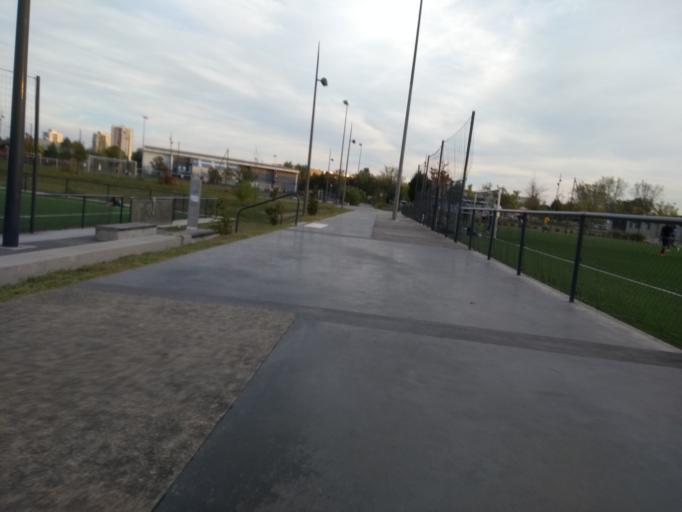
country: FR
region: Aquitaine
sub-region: Departement de la Gironde
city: Talence
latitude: 44.8023
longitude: -0.6060
